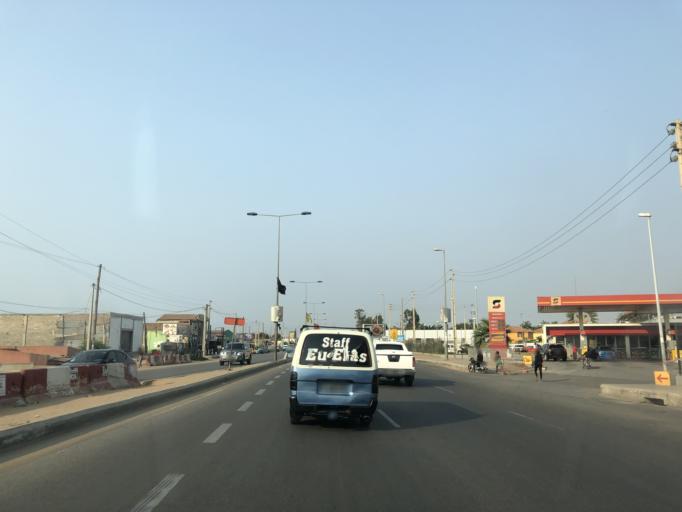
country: AO
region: Luanda
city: Luanda
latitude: -8.9128
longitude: 13.1758
